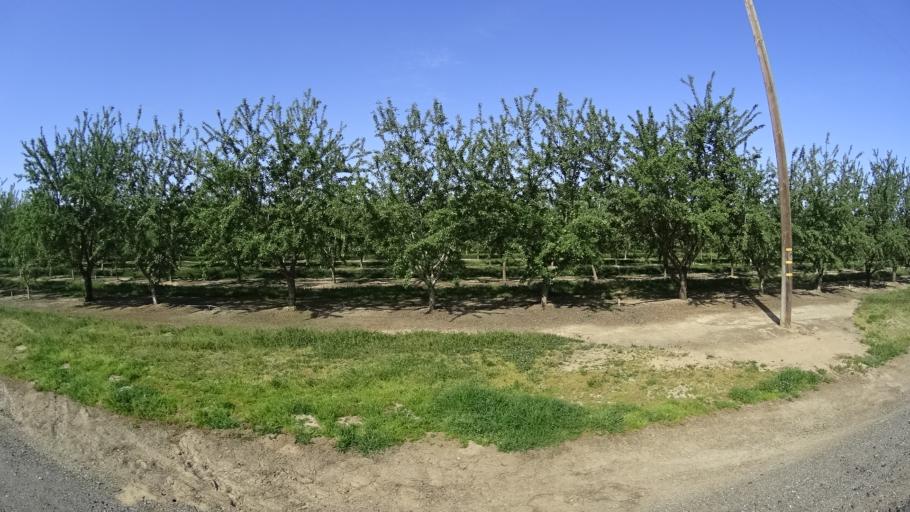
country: US
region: California
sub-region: Glenn County
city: Hamilton City
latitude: 39.6473
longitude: -122.0181
